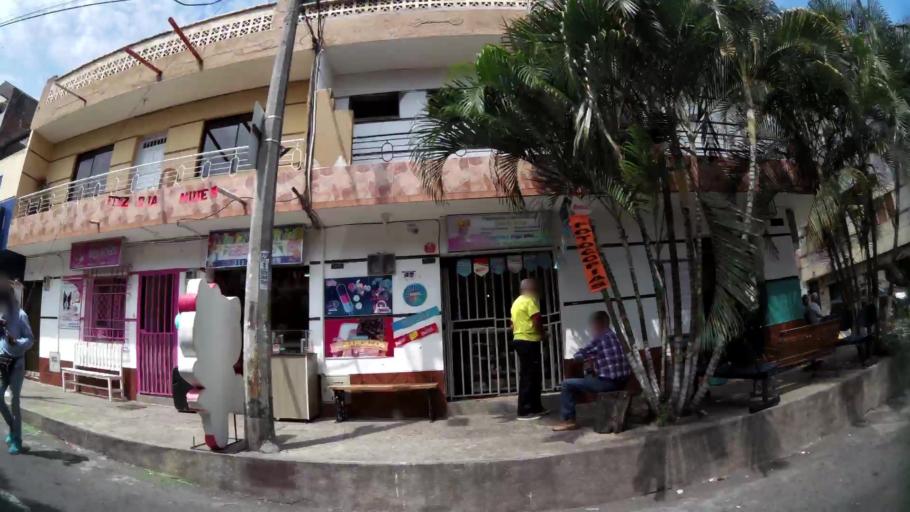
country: CO
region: Antioquia
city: Bello
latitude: 6.3200
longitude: -75.5594
